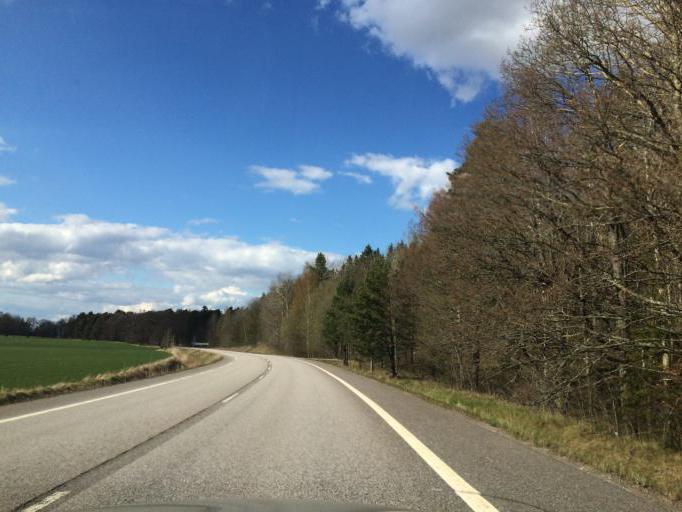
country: SE
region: Soedermanland
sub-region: Eskilstuna Kommun
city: Eskilstuna
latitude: 59.4370
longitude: 16.6303
